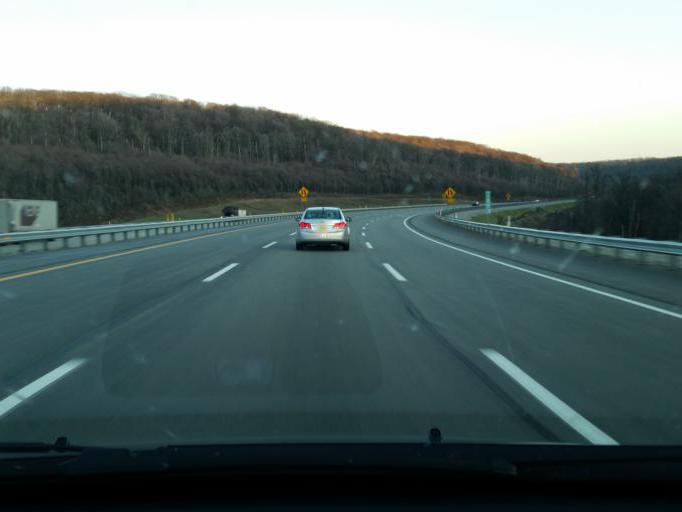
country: US
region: Pennsylvania
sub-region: Westmoreland County
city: Ligonier
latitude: 40.1013
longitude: -79.2030
